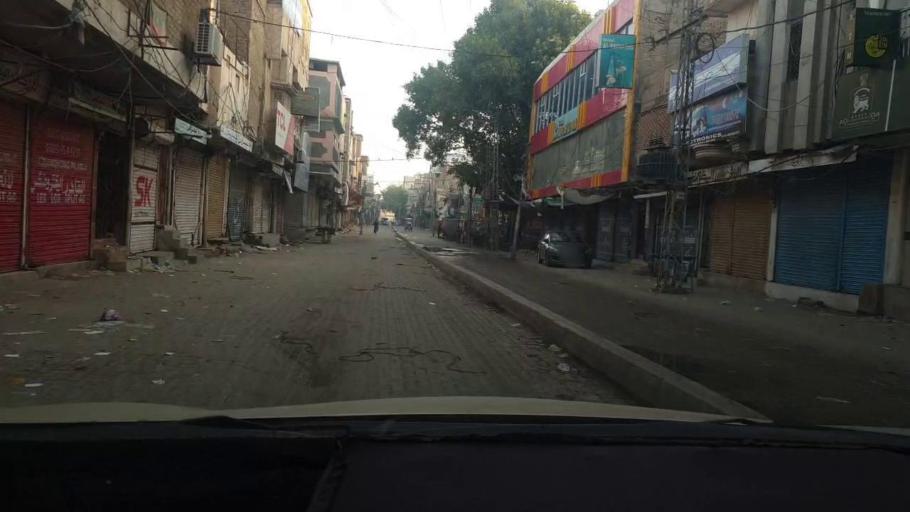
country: PK
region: Sindh
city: Larkana
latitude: 27.5534
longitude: 68.2154
